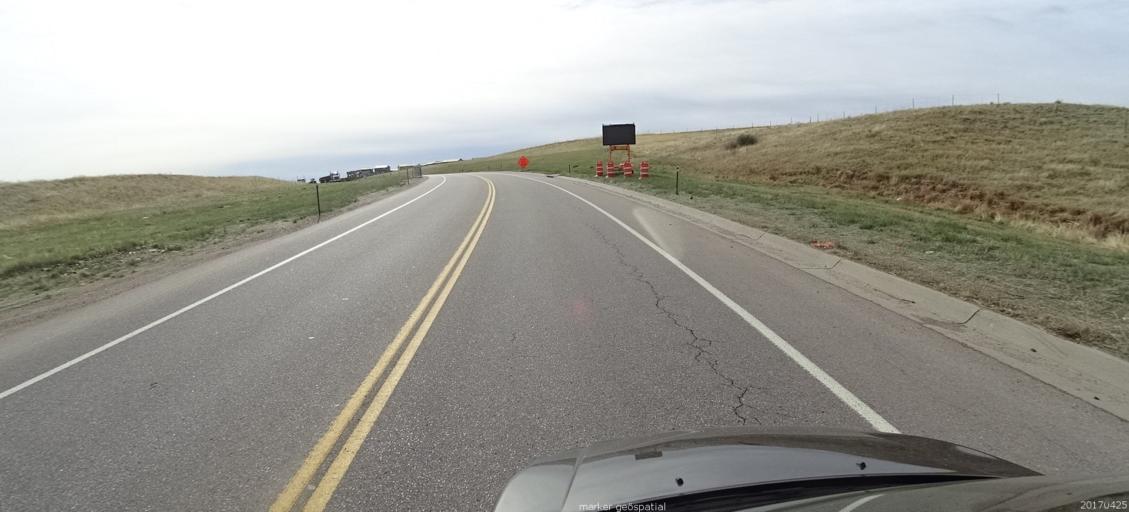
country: US
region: Colorado
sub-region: Douglas County
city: Stonegate
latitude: 39.5200
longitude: -104.8340
